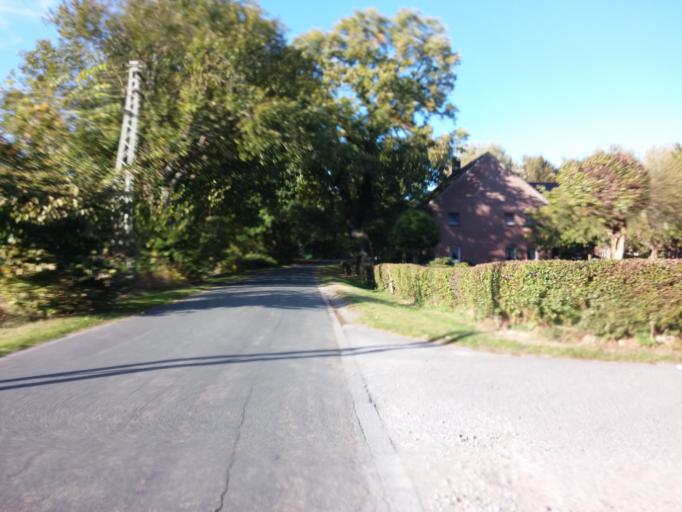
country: DE
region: North Rhine-Westphalia
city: Dorsten
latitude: 51.6466
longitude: 6.9729
